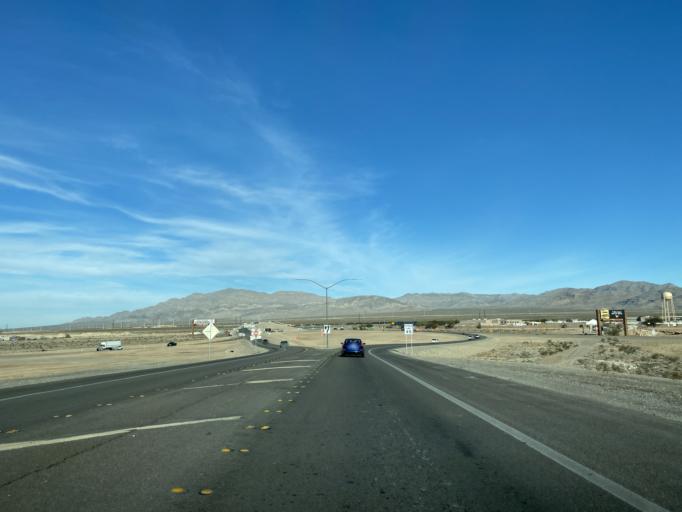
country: US
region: Nevada
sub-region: Clark County
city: Nellis Air Force Base
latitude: 36.2721
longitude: -115.0569
